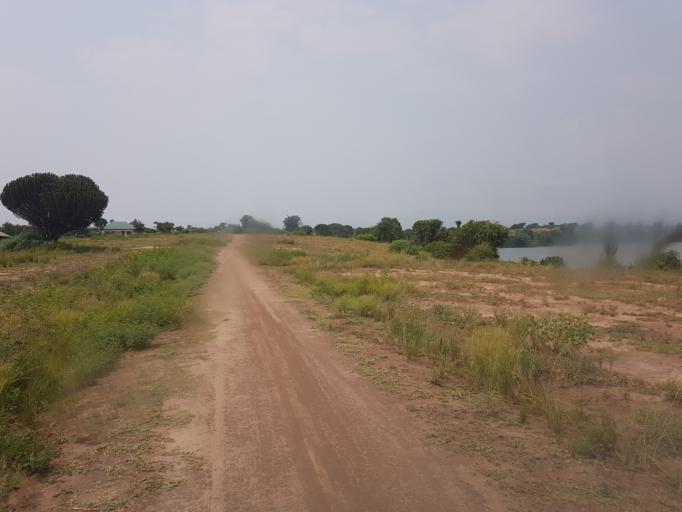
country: UG
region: Western Region
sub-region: Rubirizi District
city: Rubirizi
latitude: -0.0769
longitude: 30.1740
